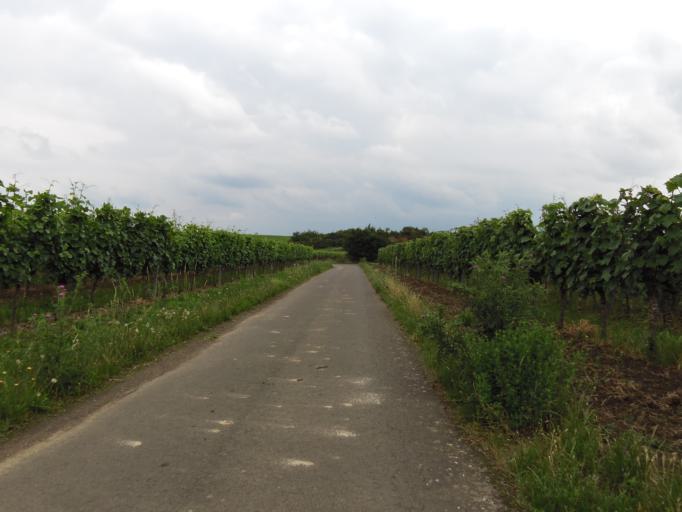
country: DE
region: Rheinland-Pfalz
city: Kallstadt
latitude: 49.4986
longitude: 8.1853
